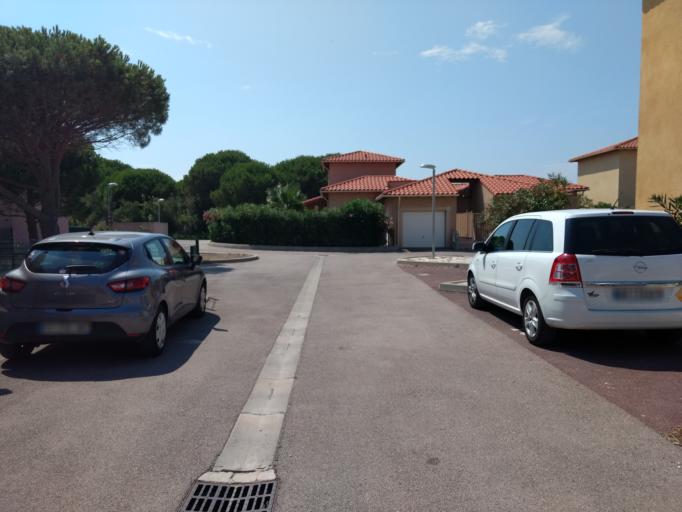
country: FR
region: Languedoc-Roussillon
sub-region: Departement des Pyrenees-Orientales
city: Le Barcares
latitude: 42.7875
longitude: 3.0306
